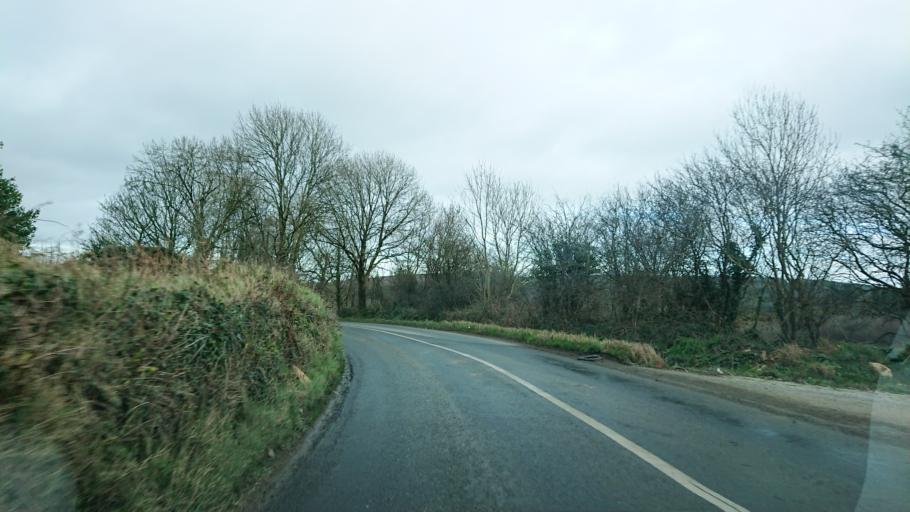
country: IE
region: Leinster
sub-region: Kilkenny
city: Mooncoin
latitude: 52.2042
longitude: -7.2542
